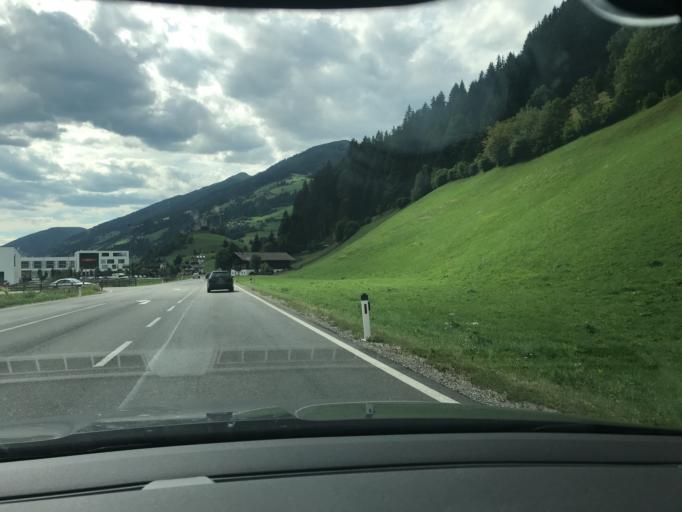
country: AT
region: Tyrol
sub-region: Politischer Bezirk Lienz
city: Heinfels
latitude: 46.7490
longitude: 12.4544
